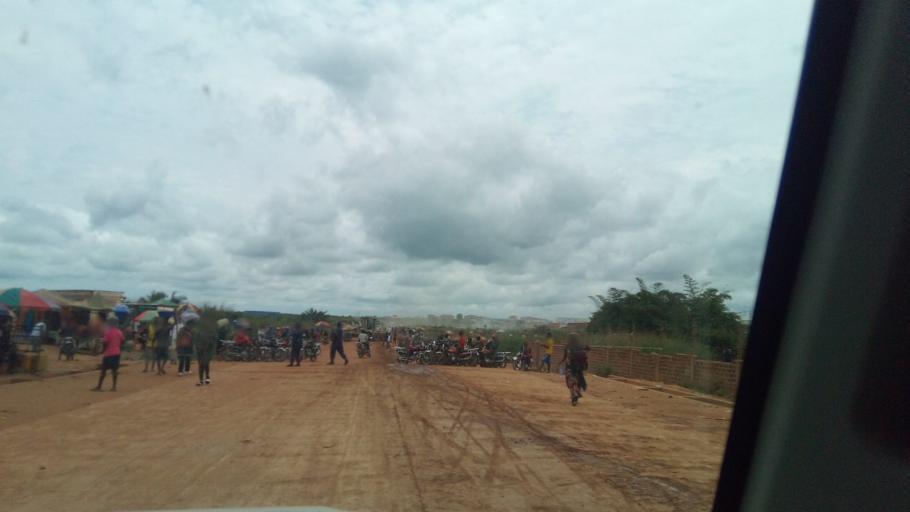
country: AO
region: Zaire
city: Mbanza Congo
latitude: -5.8419
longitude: 14.0777
